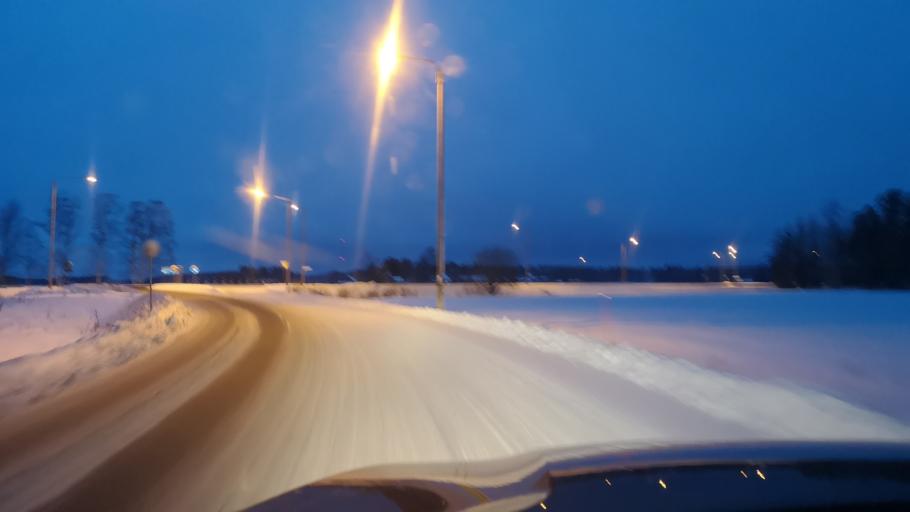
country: FI
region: Varsinais-Suomi
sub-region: Loimaa
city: Loimaa
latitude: 60.8841
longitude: 23.0894
